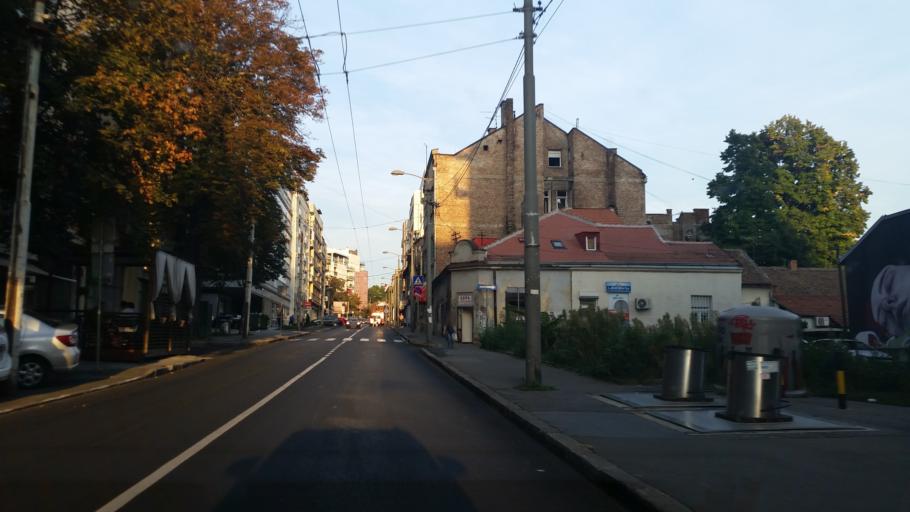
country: RS
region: Central Serbia
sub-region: Belgrade
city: Vracar
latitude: 44.7981
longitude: 20.4813
